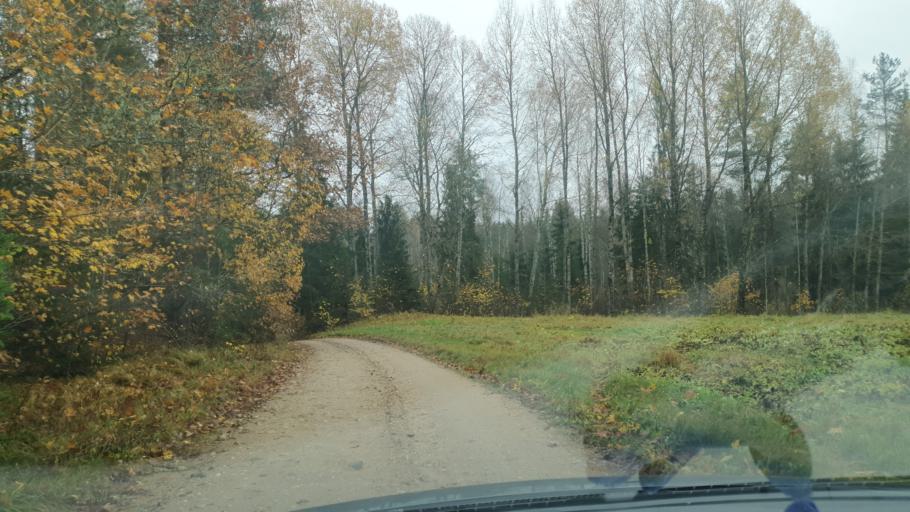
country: EE
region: Viljandimaa
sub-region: Karksi vald
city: Karksi-Nuia
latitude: 58.0051
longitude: 25.5494
